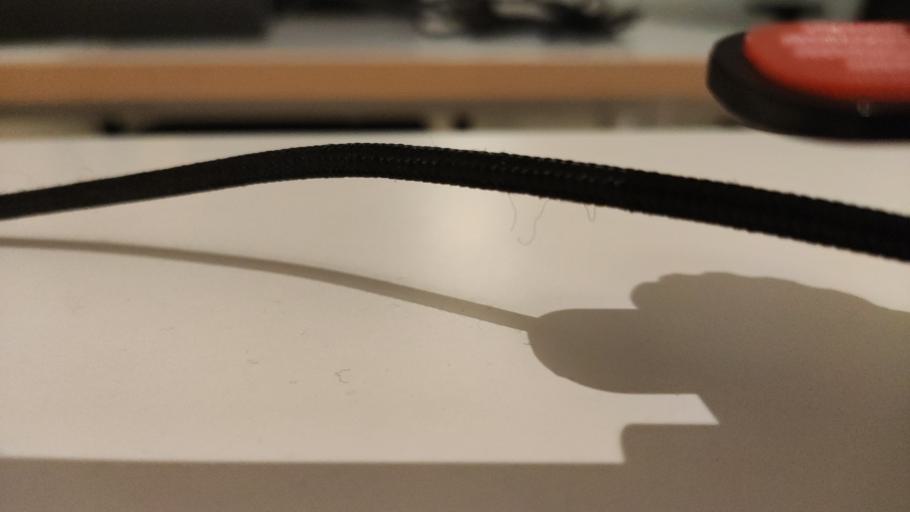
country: RU
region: Moskovskaya
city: Semkhoz
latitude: 56.4000
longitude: 38.0310
